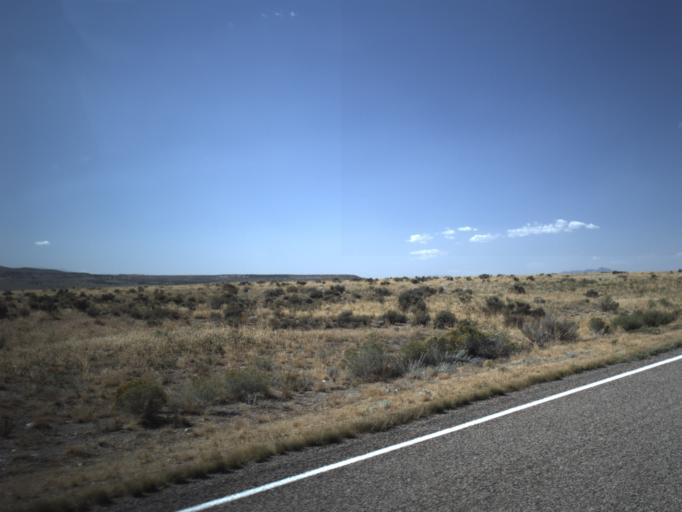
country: US
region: Utah
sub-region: Beaver County
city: Milford
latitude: 38.8088
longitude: -112.8754
